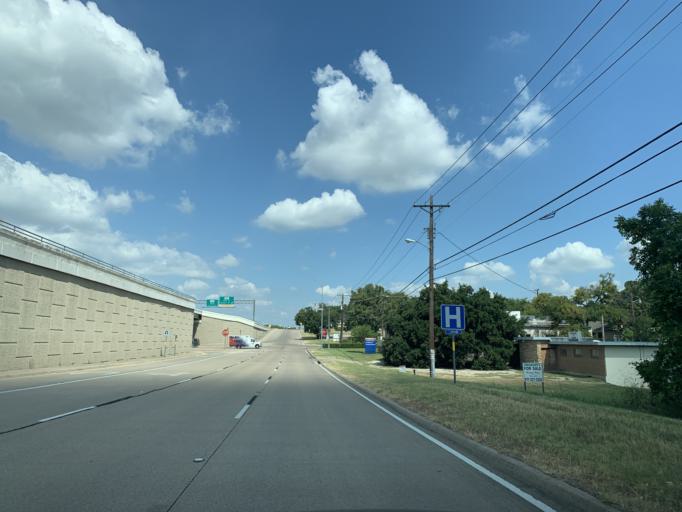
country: US
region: Texas
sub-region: Tarrant County
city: Azle
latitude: 32.8798
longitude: -97.5338
